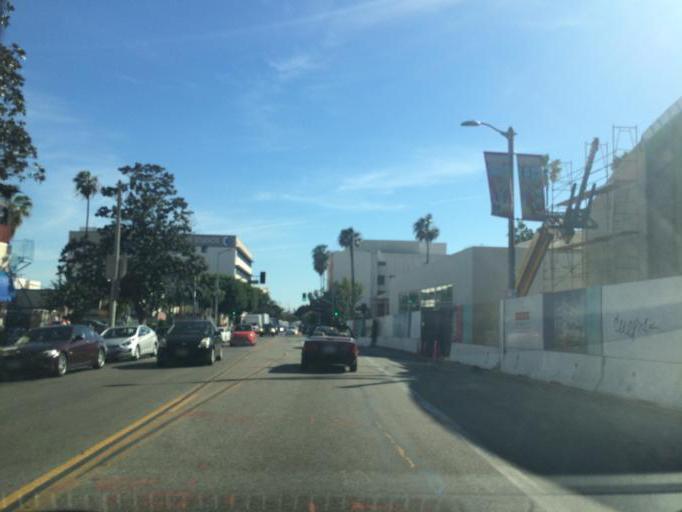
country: US
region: California
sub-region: Los Angeles County
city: Hollywood
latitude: 34.0988
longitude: -118.3223
